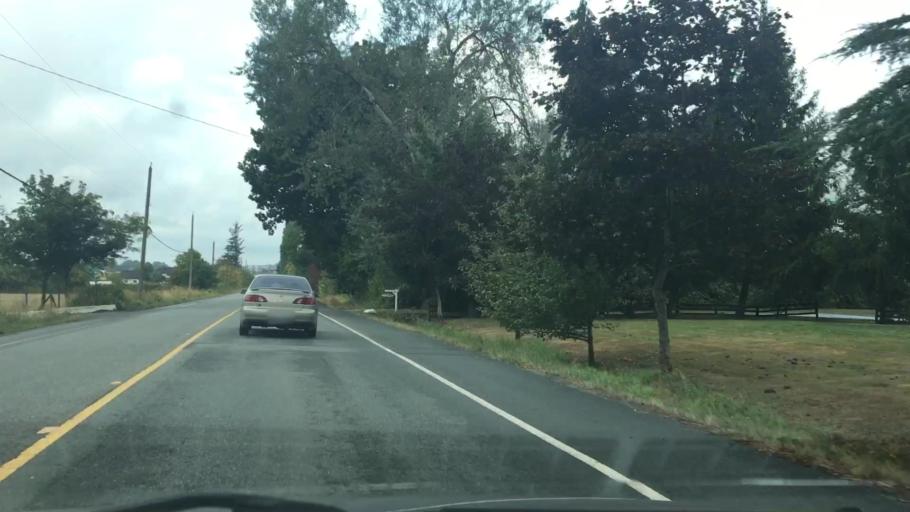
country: CA
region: British Columbia
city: Langley
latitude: 49.1044
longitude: -122.6075
